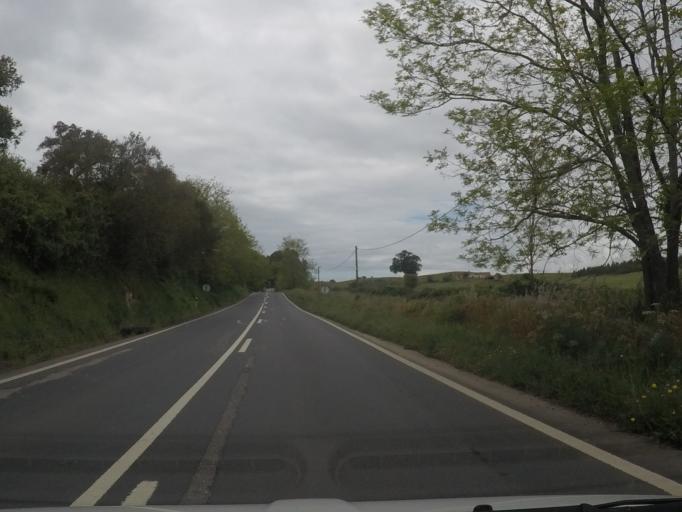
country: PT
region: Setubal
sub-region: Santiago do Cacem
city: Cercal
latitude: 37.8212
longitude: -8.6855
